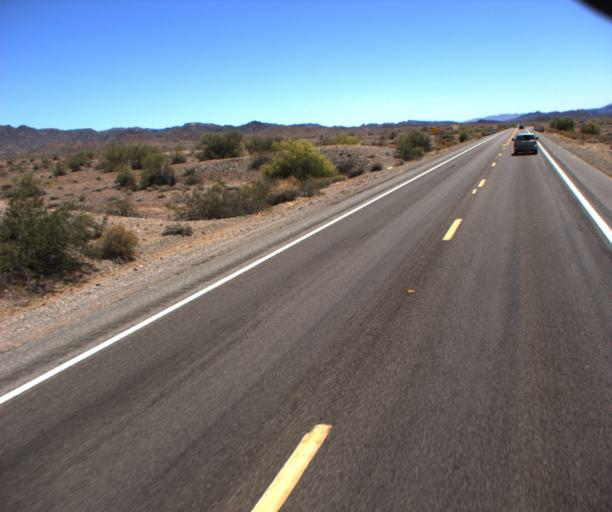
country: US
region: Arizona
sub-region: Mohave County
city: Lake Havasu City
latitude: 34.4098
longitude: -114.1888
